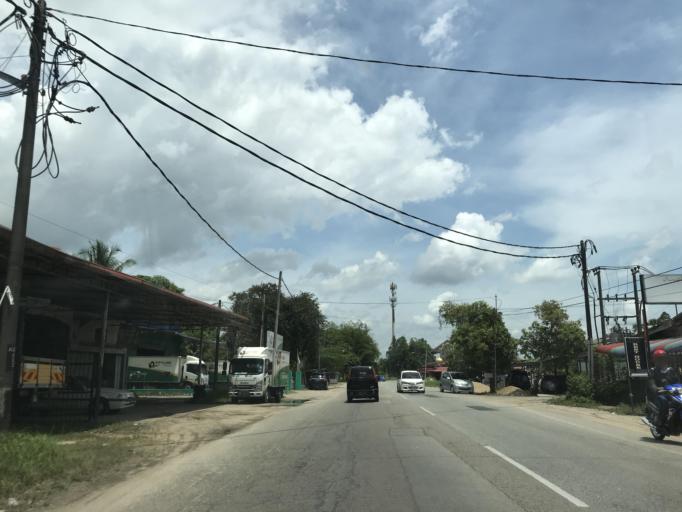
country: MY
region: Kelantan
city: Pasir Mas
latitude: 6.0508
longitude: 102.1836
